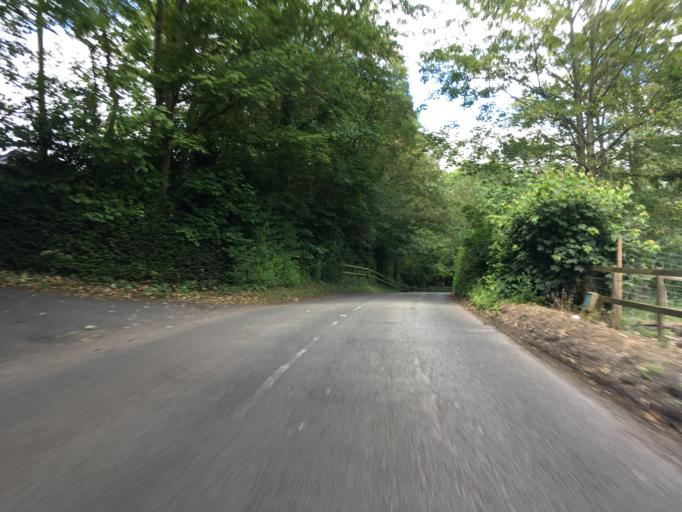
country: GB
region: England
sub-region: West Berkshire
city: Wickham
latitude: 51.4679
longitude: -1.4403
